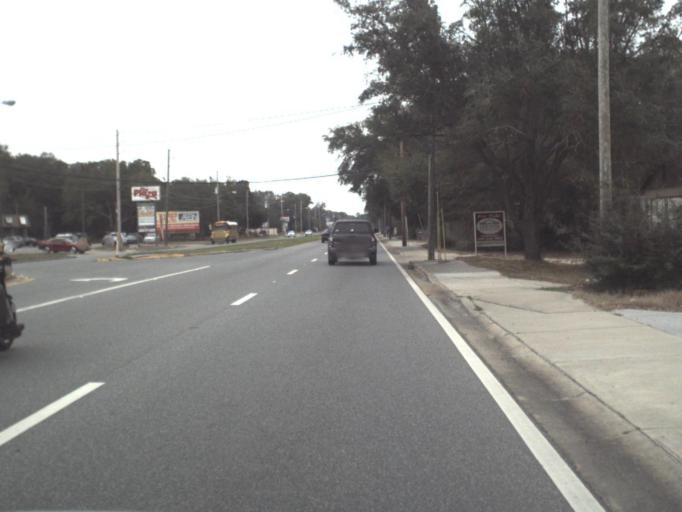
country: US
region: Florida
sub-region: Bay County
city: Parker
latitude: 30.1132
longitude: -85.6004
